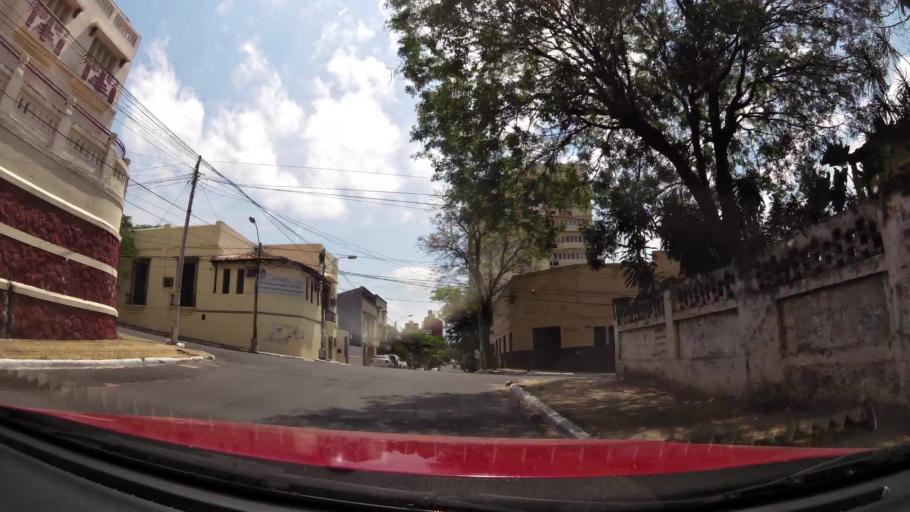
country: PY
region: Asuncion
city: Asuncion
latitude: -25.2886
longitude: -57.6323
